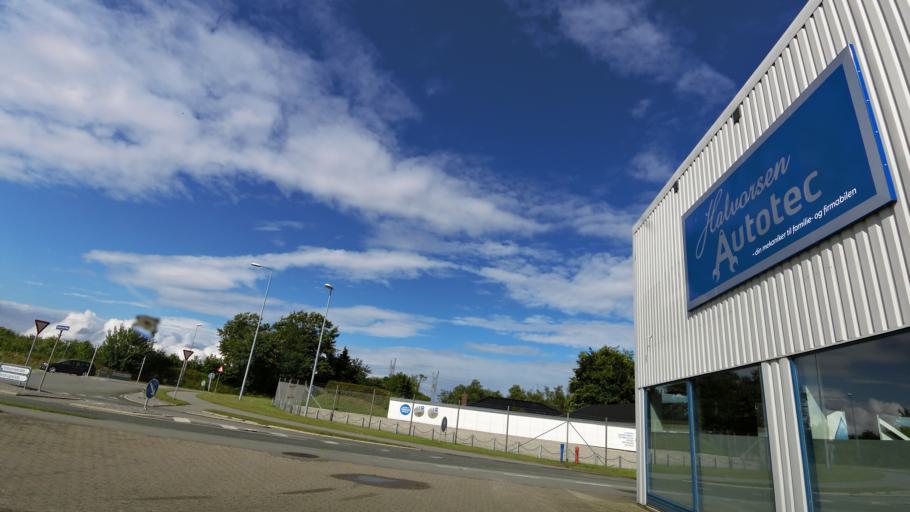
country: DK
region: South Denmark
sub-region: Assens Kommune
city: Vissenbjerg
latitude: 55.3920
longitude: 10.1419
